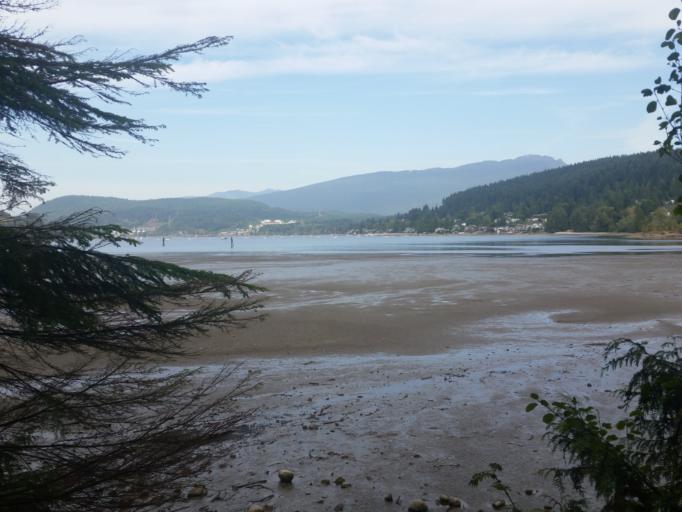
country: CA
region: British Columbia
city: Port Moody
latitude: 49.2816
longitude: -122.8401
